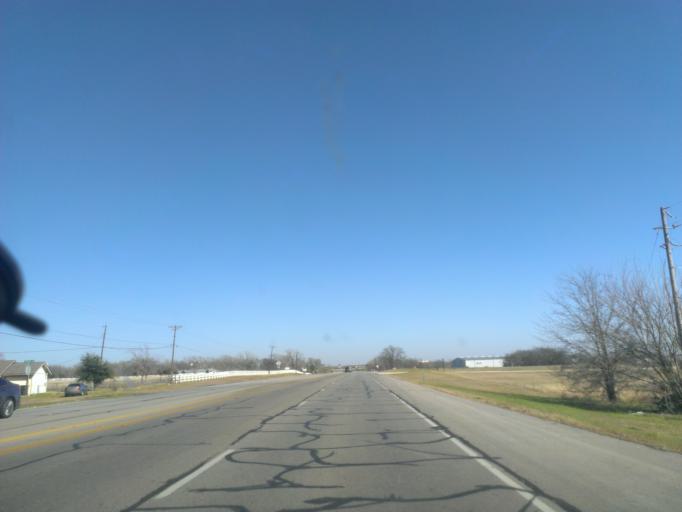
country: US
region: Texas
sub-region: Williamson County
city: Taylor
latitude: 30.5745
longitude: -97.3910
